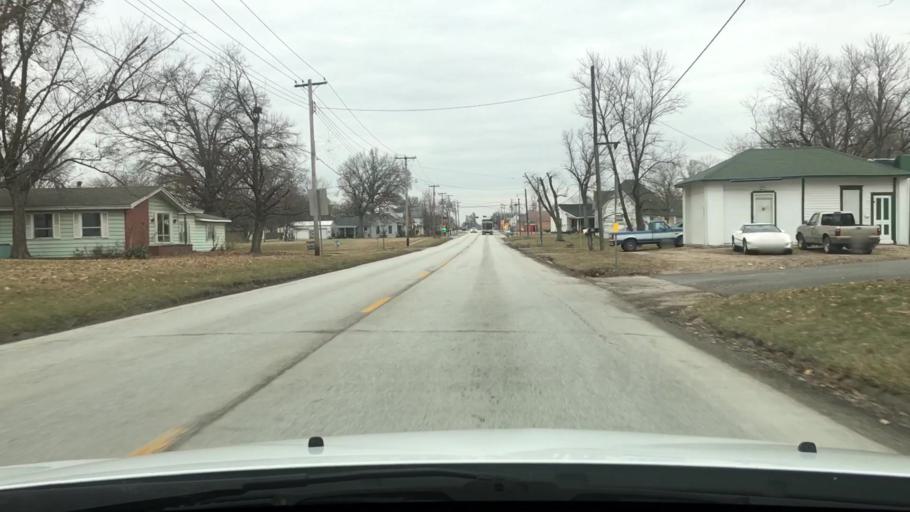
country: US
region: Missouri
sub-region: Audrain County
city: Vandalia
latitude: 39.2389
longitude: -91.6457
